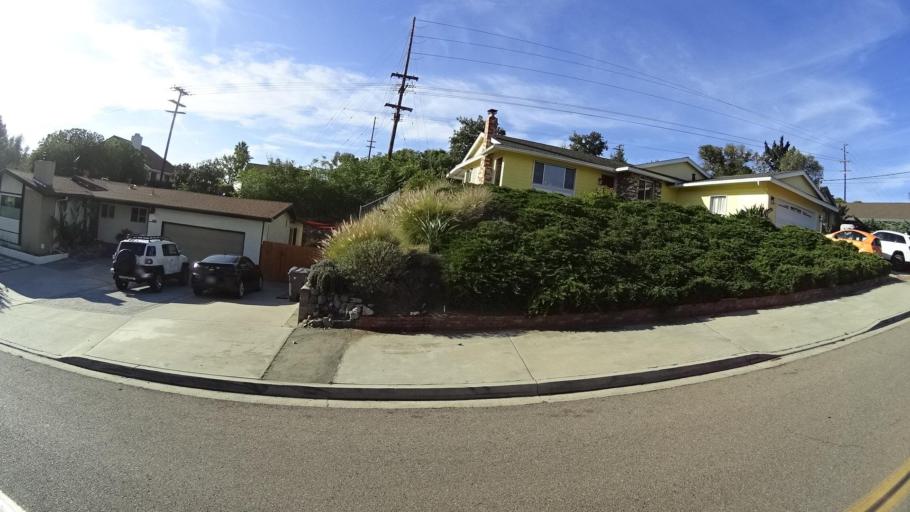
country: US
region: California
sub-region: San Diego County
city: Casa de Oro-Mount Helix
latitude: 32.7409
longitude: -116.9752
